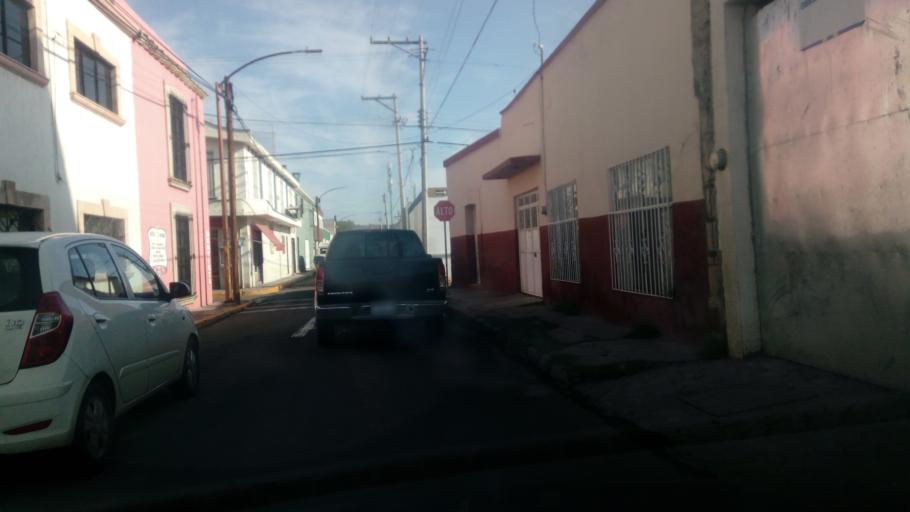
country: MX
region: Durango
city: Victoria de Durango
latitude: 24.0329
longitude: -104.6643
